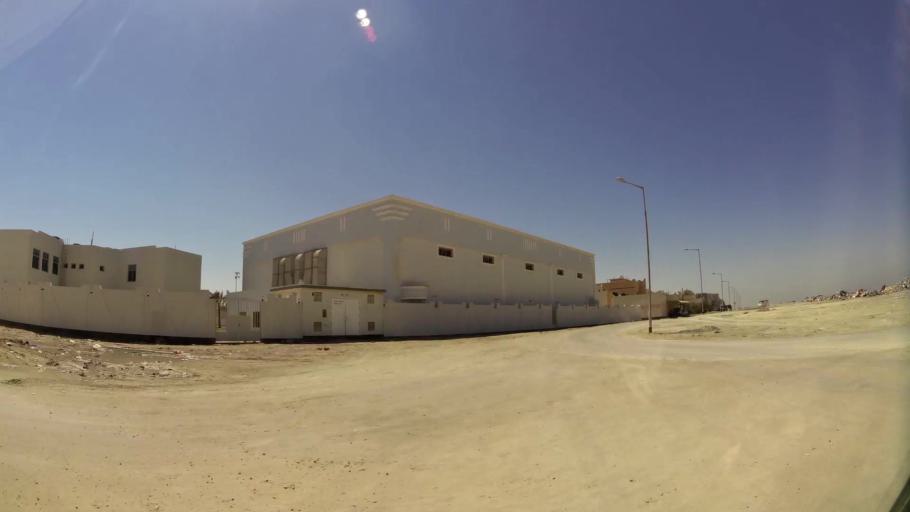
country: BH
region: Muharraq
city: Al Muharraq
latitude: 26.2881
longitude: 50.6255
